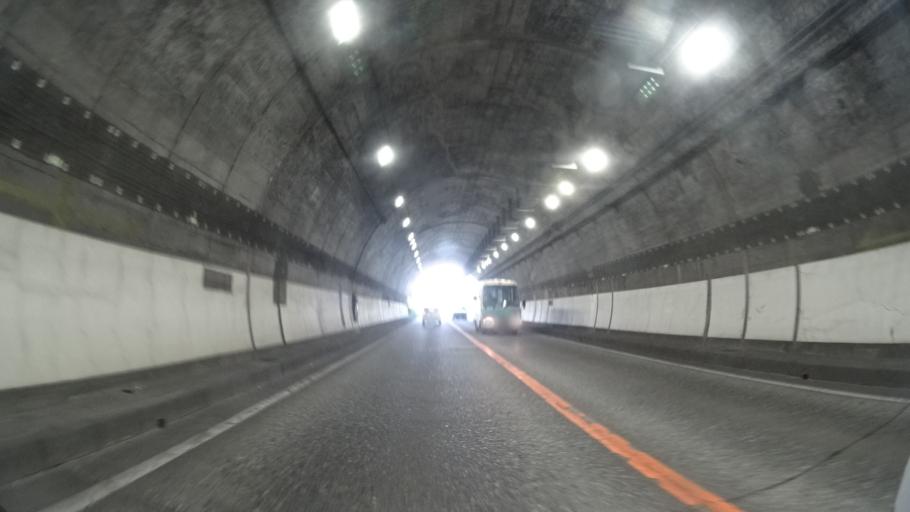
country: JP
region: Tottori
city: Tottori
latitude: 35.5214
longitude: 134.1004
